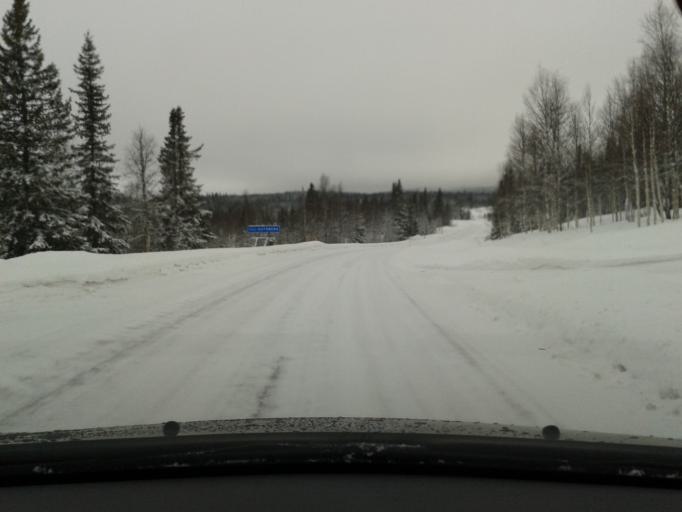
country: SE
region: Vaesterbotten
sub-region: Vilhelmina Kommun
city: Sjoberg
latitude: 65.1823
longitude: 15.9034
